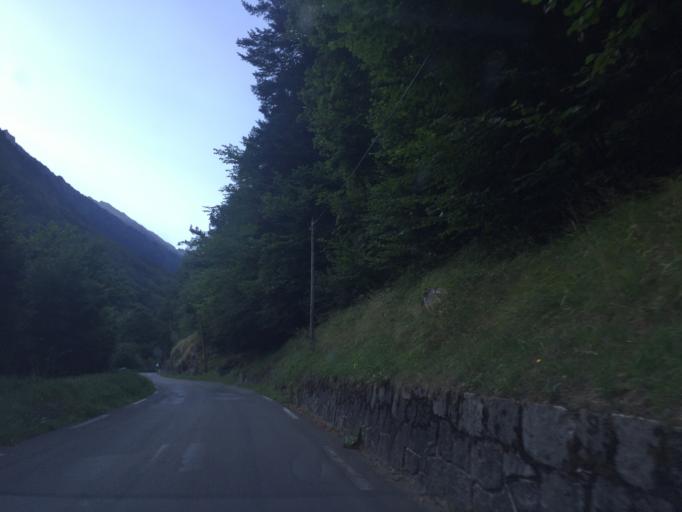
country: FR
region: Midi-Pyrenees
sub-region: Departement des Hautes-Pyrenees
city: Cauterets
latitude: 42.8779
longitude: -0.1108
